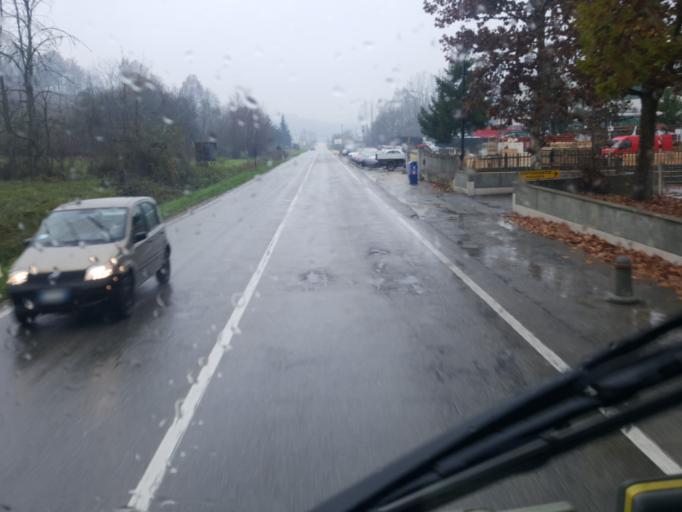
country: IT
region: Piedmont
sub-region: Provincia di Cuneo
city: Vezza d'Alba
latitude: 44.7760
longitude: 8.0074
